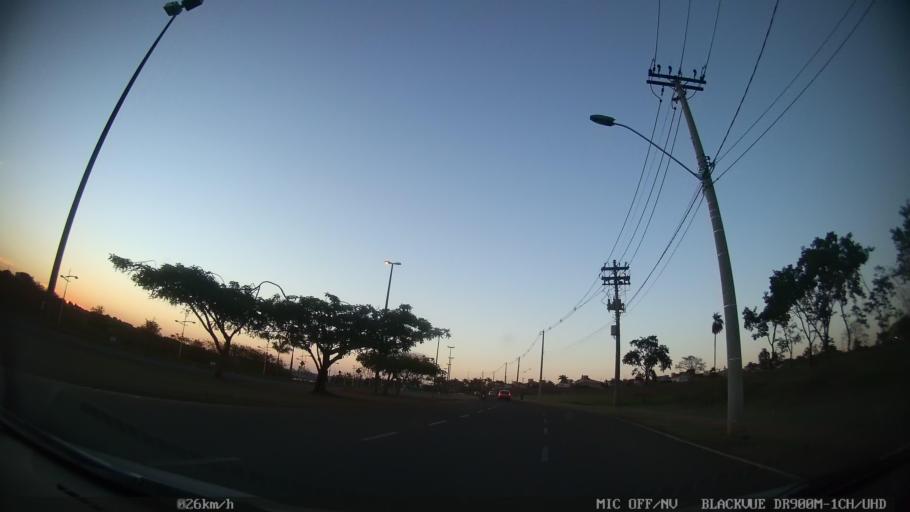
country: BR
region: Sao Paulo
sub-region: Sao Jose Do Rio Preto
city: Sao Jose do Rio Preto
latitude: -20.8239
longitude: -49.3442
